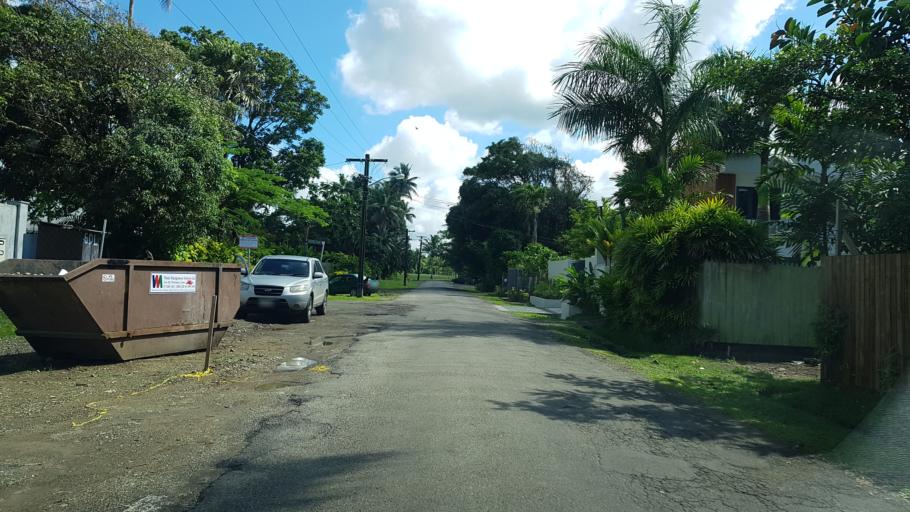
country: FJ
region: Central
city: Suva
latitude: -18.1473
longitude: 178.4554
